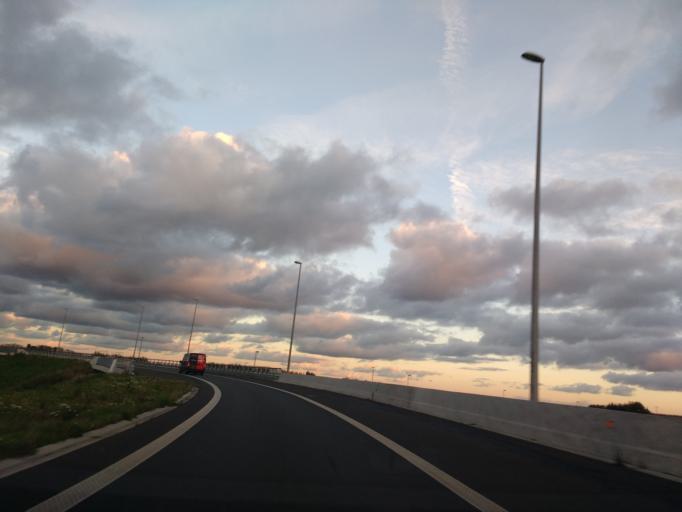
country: NL
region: Zeeland
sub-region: Gemeente Sluis
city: Sluis
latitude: 51.3053
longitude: 3.3220
